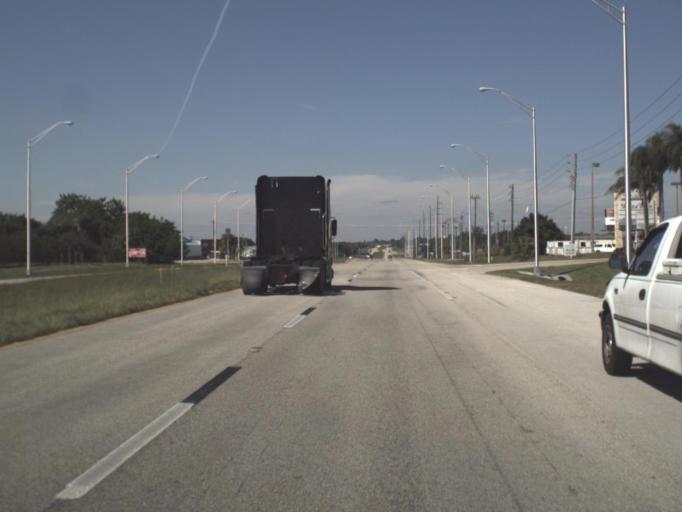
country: US
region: Florida
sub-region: Highlands County
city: Lake Placid
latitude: 27.2647
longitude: -81.3466
